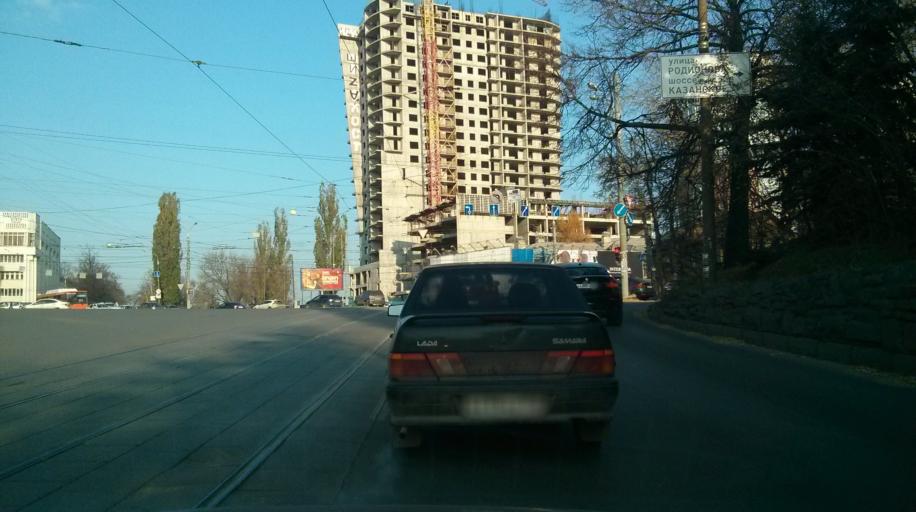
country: RU
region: Nizjnij Novgorod
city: Nizhniy Novgorod
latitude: 56.3220
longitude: 44.0336
